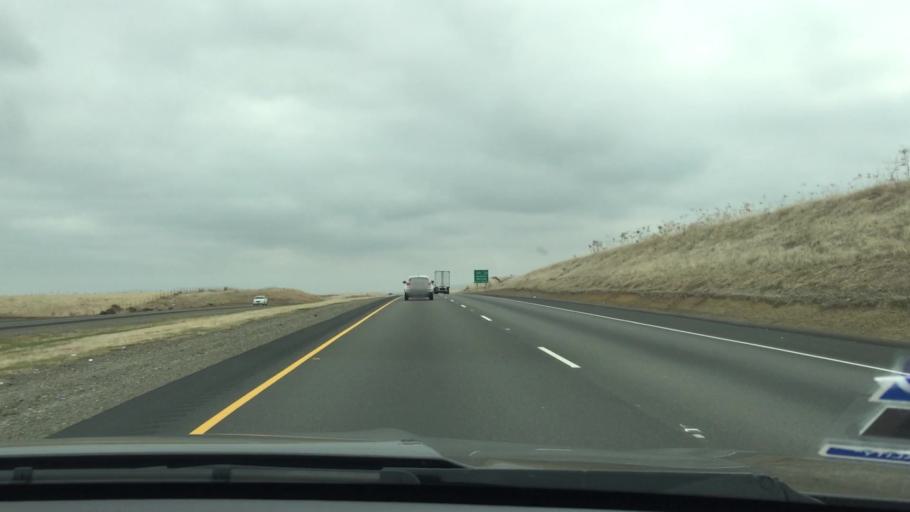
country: US
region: California
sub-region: Stanislaus County
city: Newman
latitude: 37.2662
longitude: -121.0941
